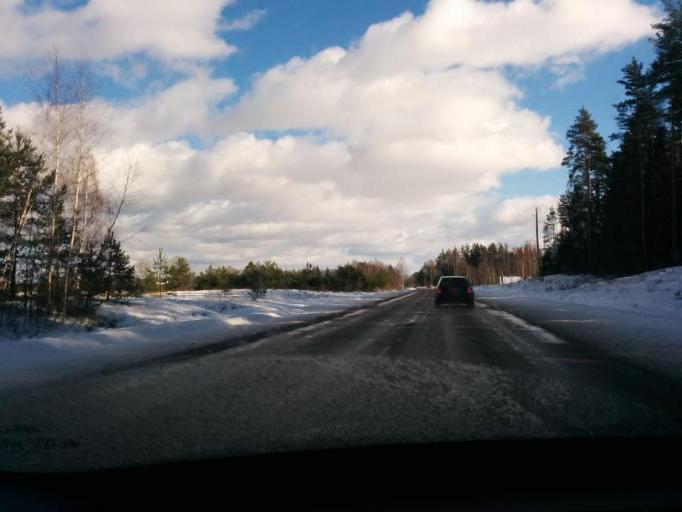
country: LV
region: Cesvaine
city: Cesvaine
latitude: 57.2381
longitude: 26.3401
